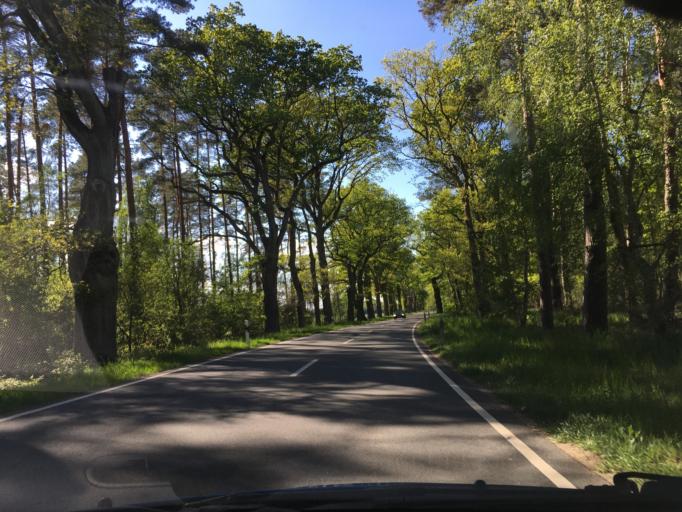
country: DE
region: Lower Saxony
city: Gartow
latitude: 53.0192
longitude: 11.5003
